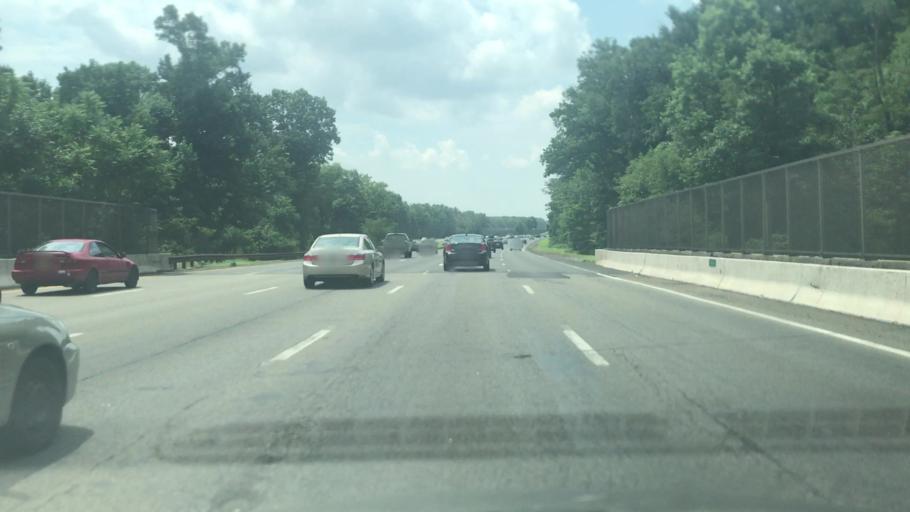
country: US
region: New Jersey
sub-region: Middlesex County
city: Iselin
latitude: 40.6061
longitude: -74.3145
